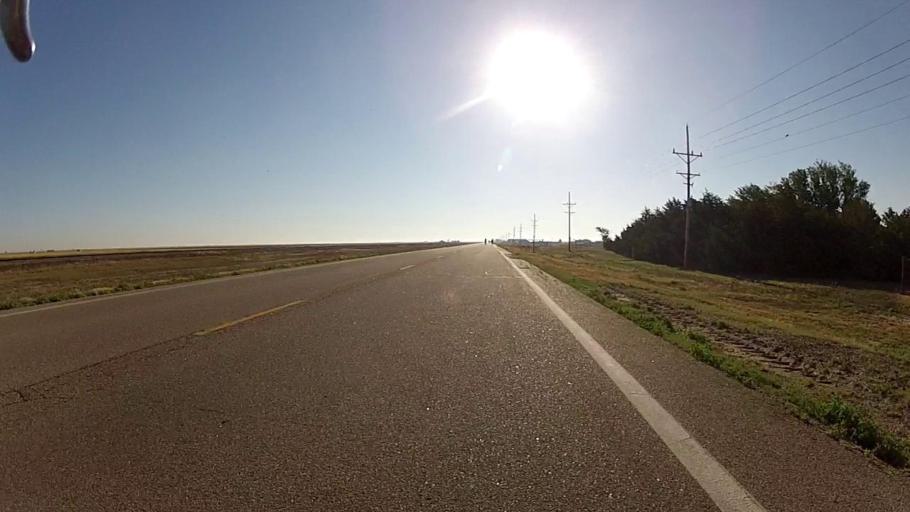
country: US
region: Kansas
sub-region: Haskell County
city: Sublette
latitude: 37.4931
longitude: -100.8090
